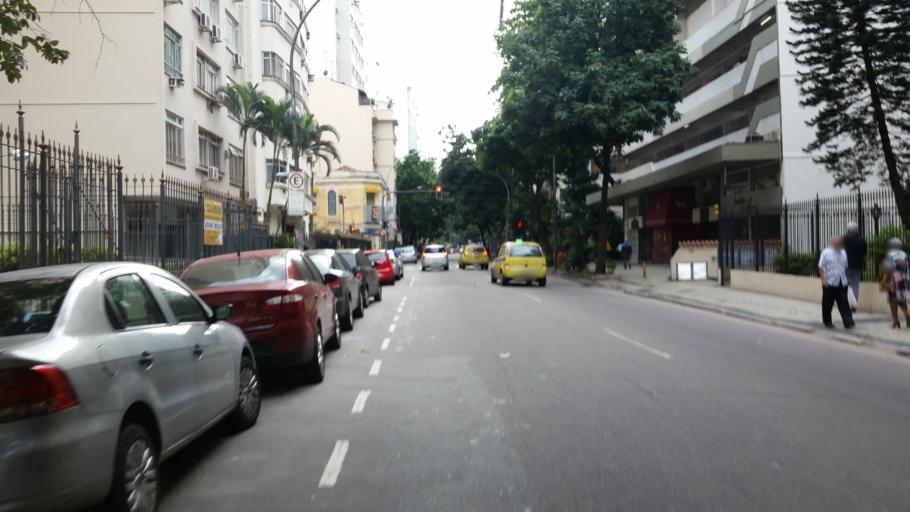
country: BR
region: Rio de Janeiro
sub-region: Rio De Janeiro
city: Rio de Janeiro
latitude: -22.9390
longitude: -43.1767
